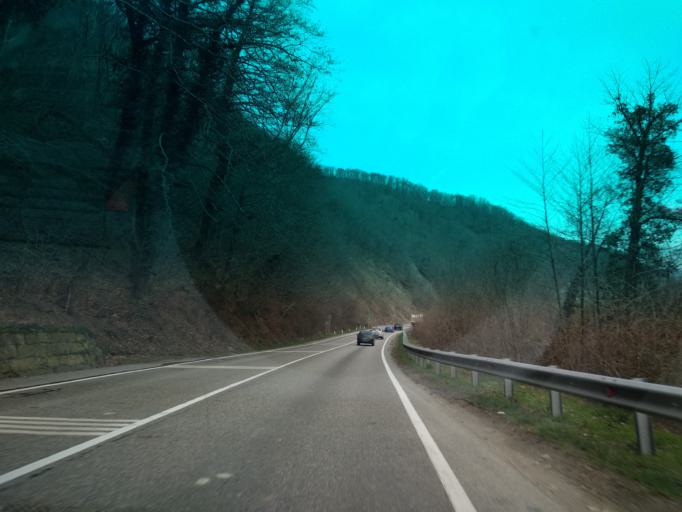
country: RU
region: Krasnodarskiy
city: Ol'ginka
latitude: 44.2231
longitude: 38.8947
